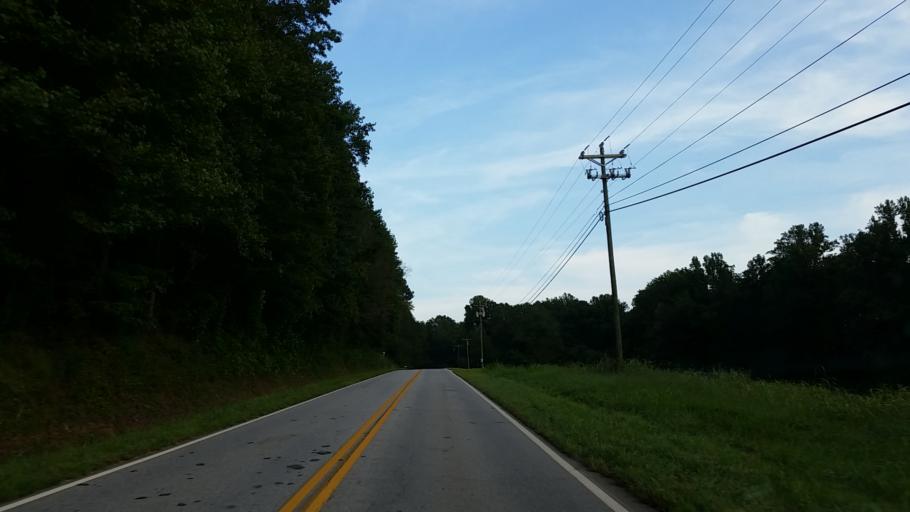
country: US
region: Georgia
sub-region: Lumpkin County
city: Dahlonega
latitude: 34.5646
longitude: -84.0042
